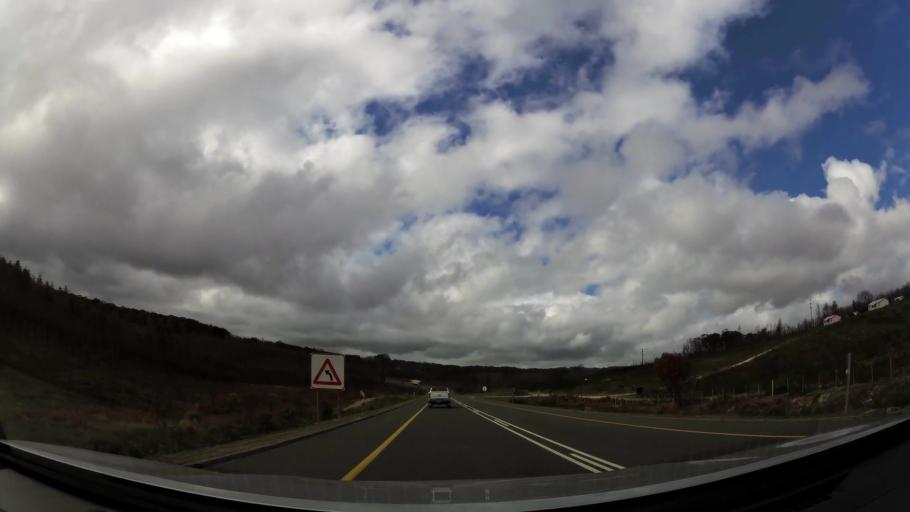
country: ZA
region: Western Cape
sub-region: Eden District Municipality
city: Knysna
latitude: -34.0365
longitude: 23.1522
